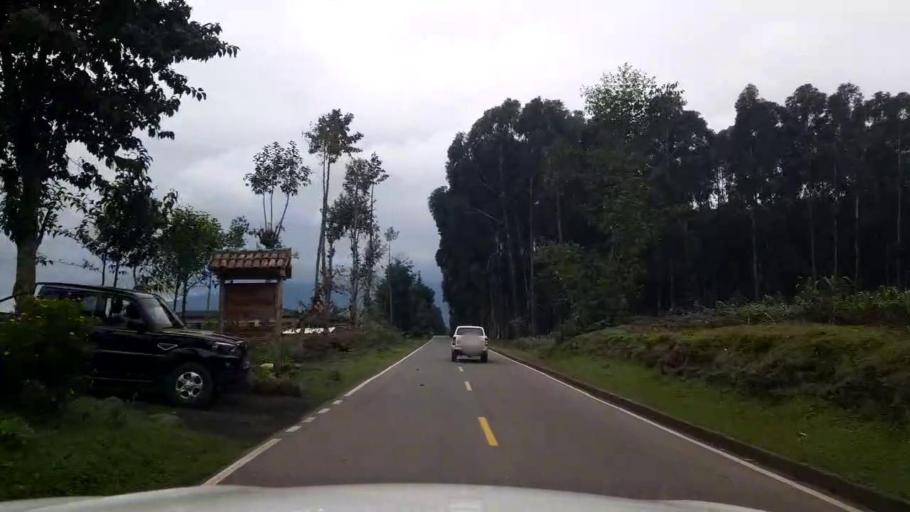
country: RW
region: Northern Province
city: Musanze
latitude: -1.4319
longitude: 29.5594
